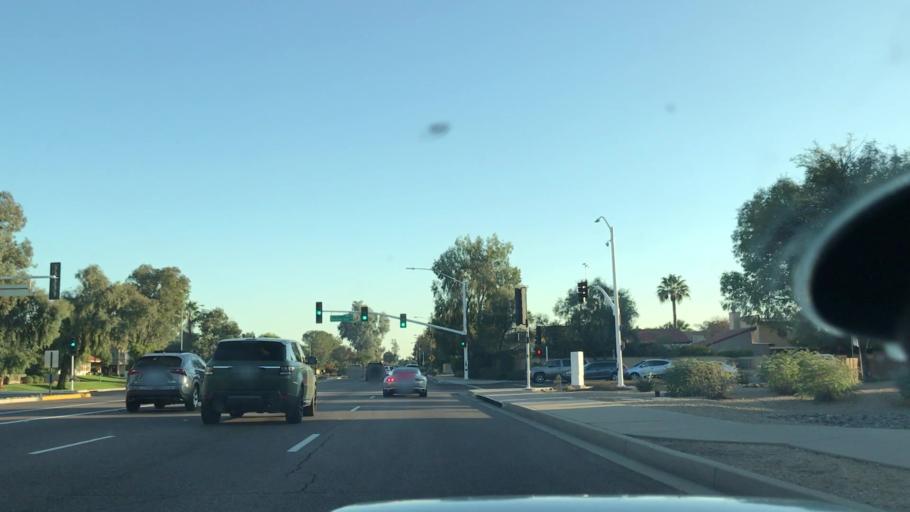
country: US
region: Arizona
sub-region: Maricopa County
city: Paradise Valley
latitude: 33.5757
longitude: -111.9066
